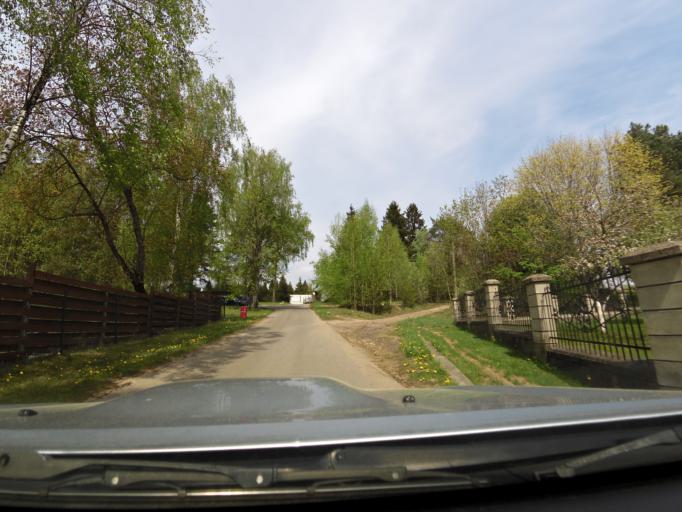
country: LT
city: Salcininkai
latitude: 54.4373
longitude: 25.3000
